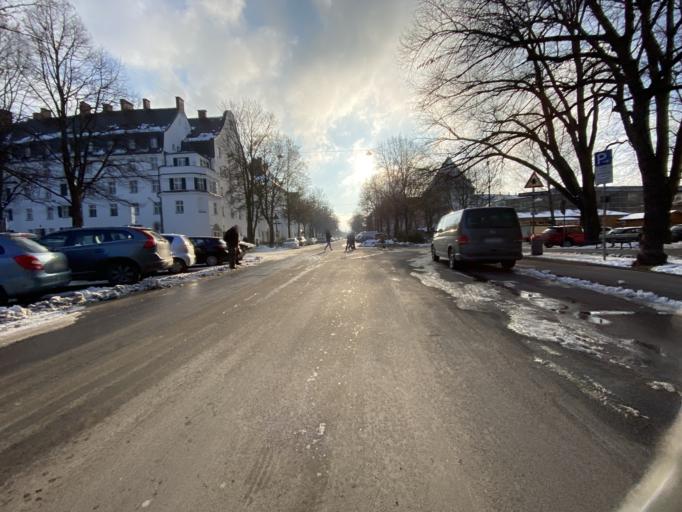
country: DE
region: Bavaria
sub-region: Upper Bavaria
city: Munich
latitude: 48.1154
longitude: 11.5511
